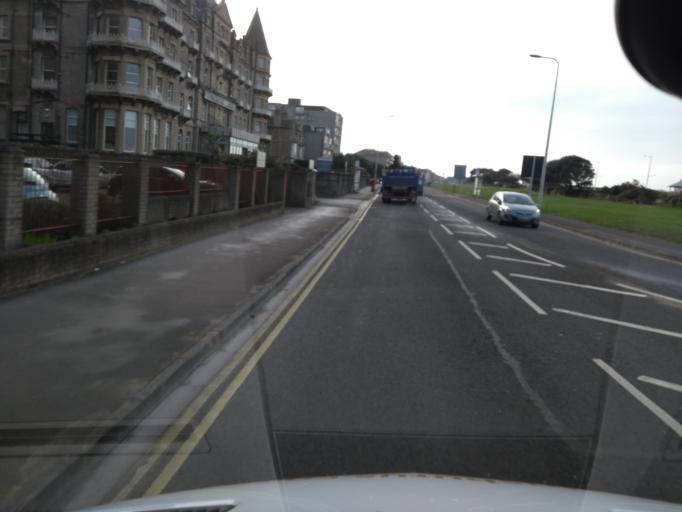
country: GB
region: England
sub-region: North Somerset
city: Weston-super-Mare
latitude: 51.3445
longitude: -2.9806
